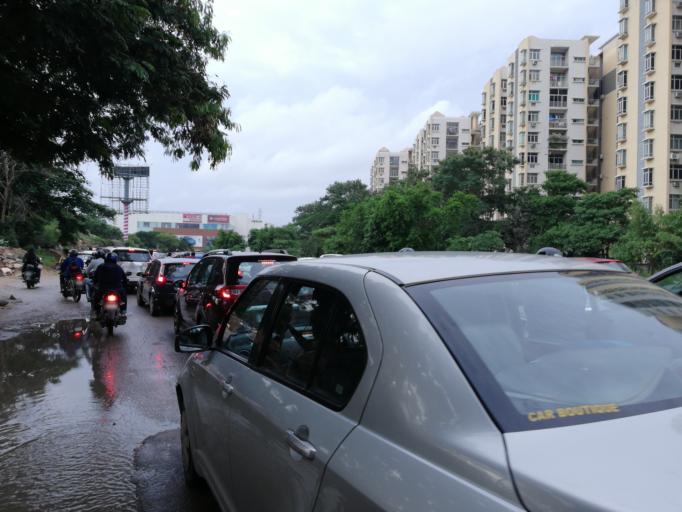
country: IN
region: Telangana
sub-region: Rangareddi
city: Kukatpalli
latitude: 17.4806
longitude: 78.3896
